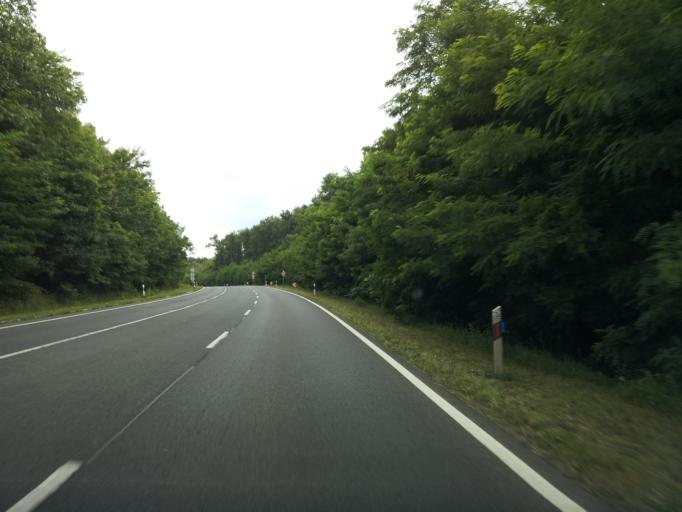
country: HU
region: Vas
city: Sarvar
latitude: 47.1064
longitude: 16.9782
